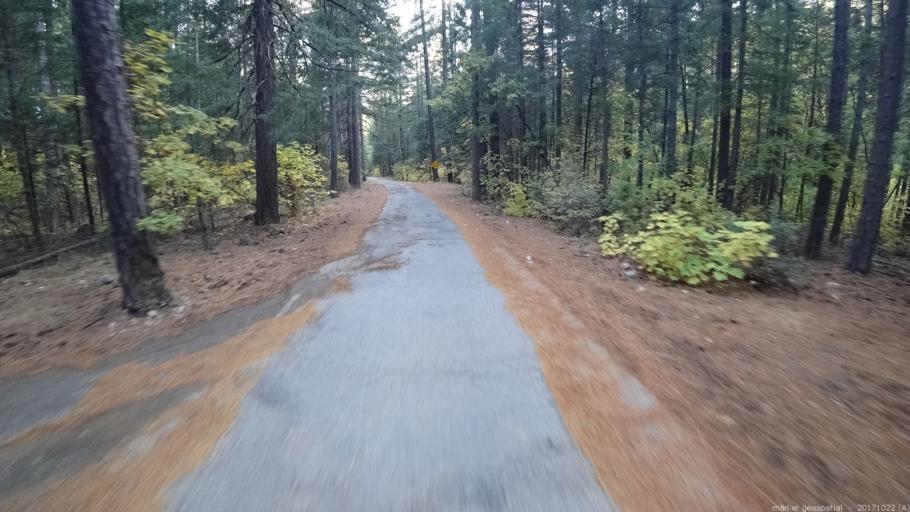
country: US
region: California
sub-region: Siskiyou County
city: Dunsmuir
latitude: 41.1703
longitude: -122.2713
